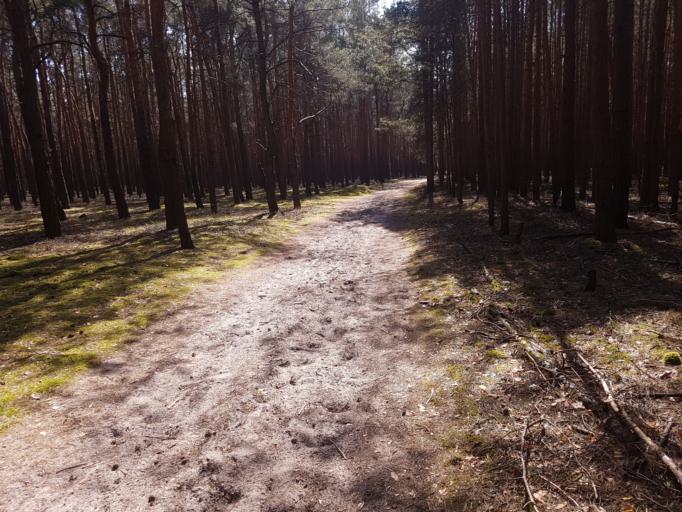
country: DE
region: Brandenburg
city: Bruck
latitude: 52.1748
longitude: 12.7571
